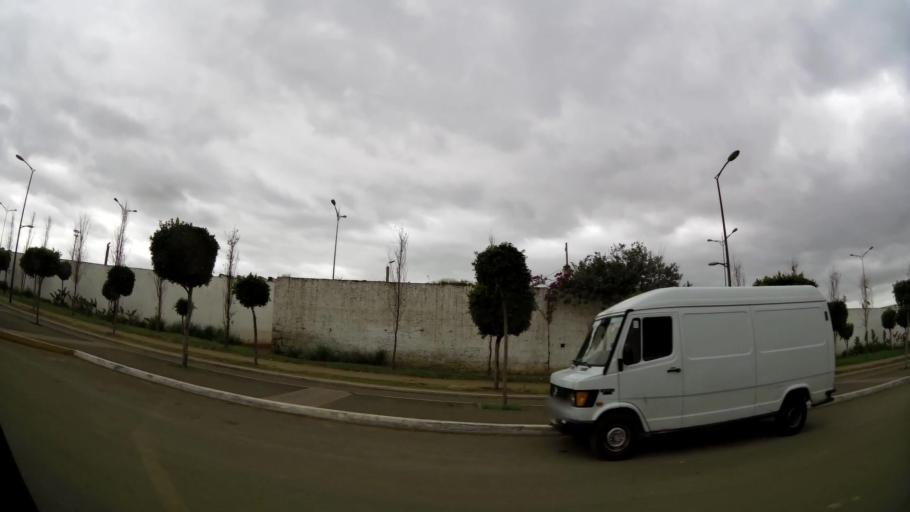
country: MA
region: Grand Casablanca
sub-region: Casablanca
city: Casablanca
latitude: 33.5547
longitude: -7.5562
